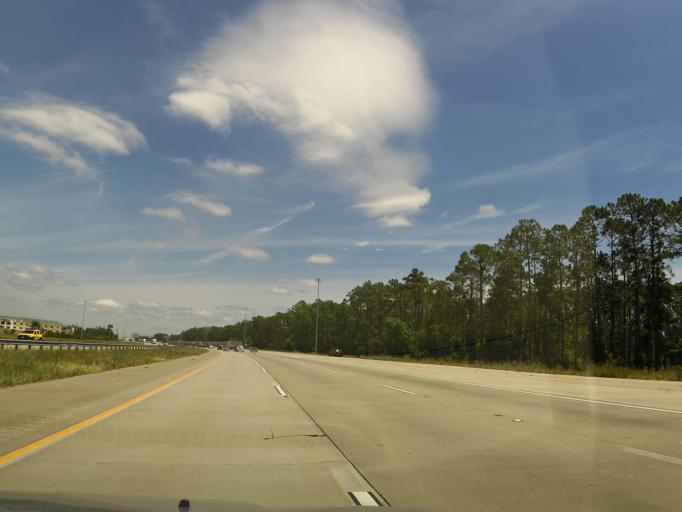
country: US
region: Georgia
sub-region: Glynn County
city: Dock Junction
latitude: 31.2425
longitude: -81.5020
